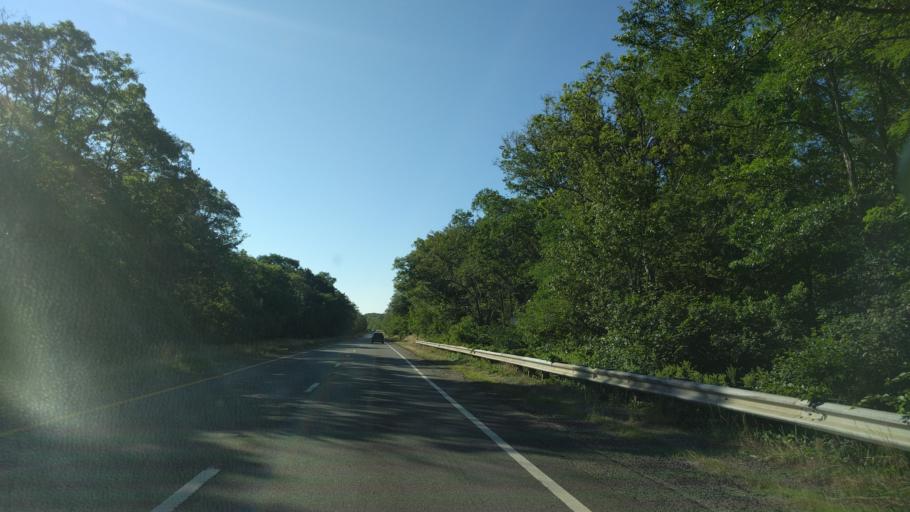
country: US
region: Massachusetts
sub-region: Barnstable County
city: West Barnstable
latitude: 41.6944
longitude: -70.3813
